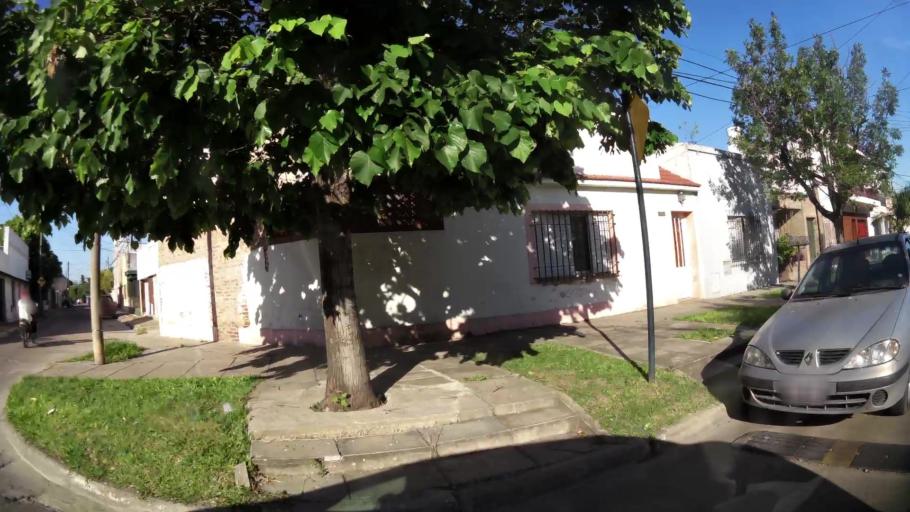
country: AR
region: Santa Fe
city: Santa Fe de la Vera Cruz
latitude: -31.6118
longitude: -60.6962
